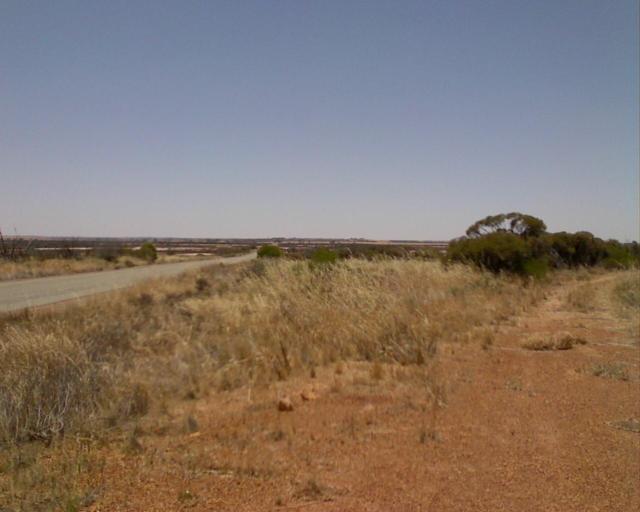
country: AU
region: Western Australia
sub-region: Wongan-Ballidu
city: Wongan Hills
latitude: -30.3669
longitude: 117.1813
